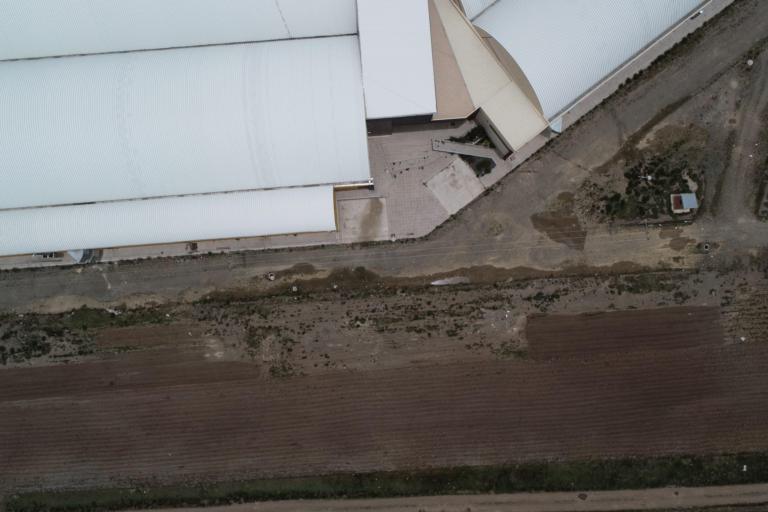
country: BO
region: La Paz
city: La Paz
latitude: -16.5197
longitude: -68.3000
